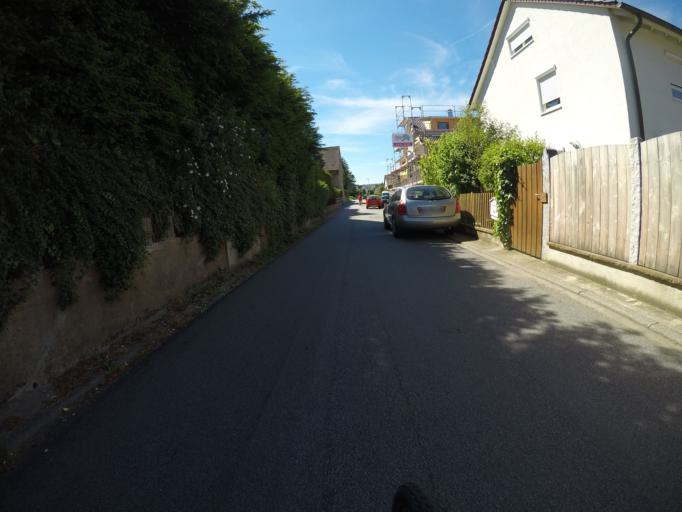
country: DE
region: Baden-Wuerttemberg
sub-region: Karlsruhe Region
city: Konigsbach-Stein
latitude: 48.9482
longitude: 8.6262
